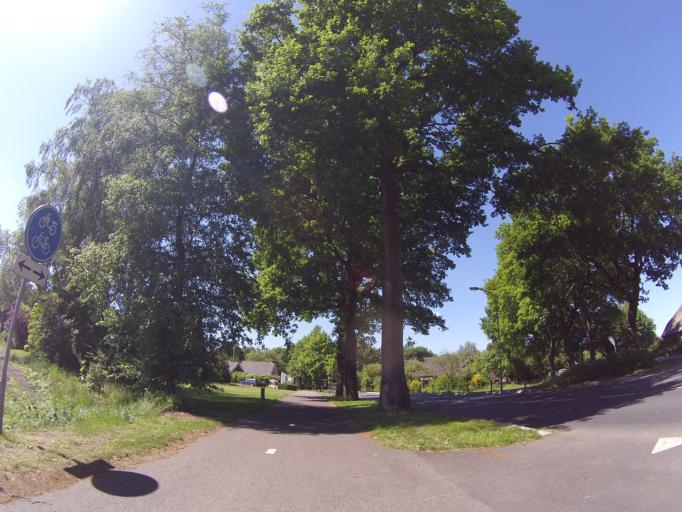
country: NL
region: Drenthe
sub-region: Gemeente Coevorden
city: Dalen
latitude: 52.7832
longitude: 6.7027
